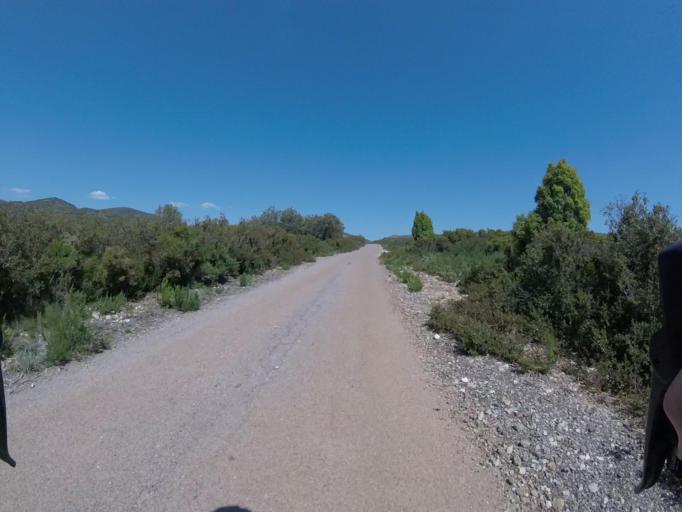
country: ES
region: Valencia
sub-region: Provincia de Castello
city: Sierra-Engarceran
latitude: 40.2414
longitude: -0.0264
